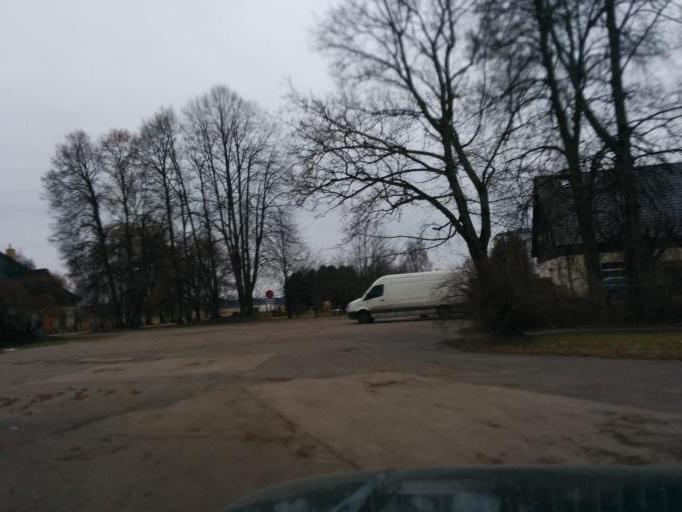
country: LV
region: Babite
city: Pinki
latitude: 56.9728
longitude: 23.8533
